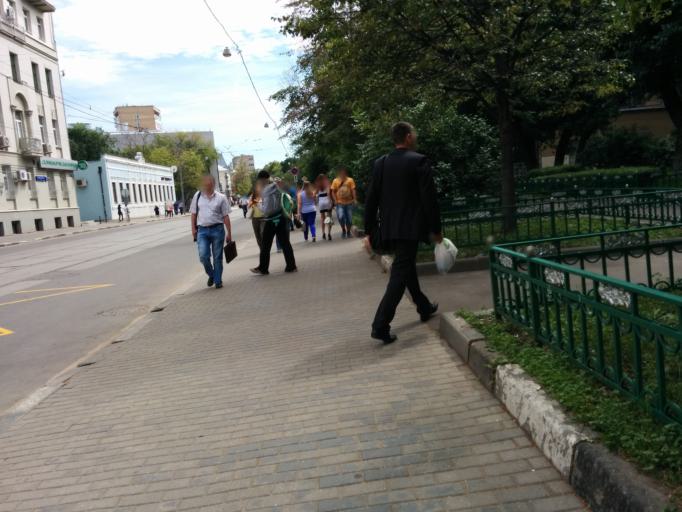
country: RU
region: Moscow
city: Zamoskvorech'ye
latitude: 55.7403
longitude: 37.6297
